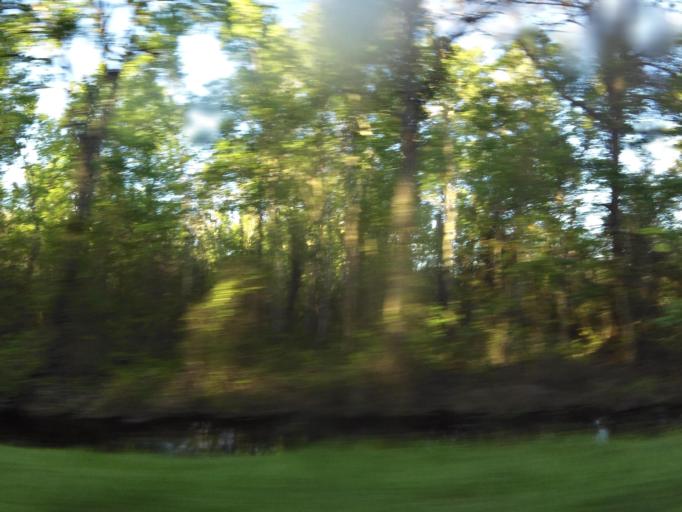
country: US
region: Florida
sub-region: Clay County
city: Keystone Heights
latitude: 29.8495
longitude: -82.0892
